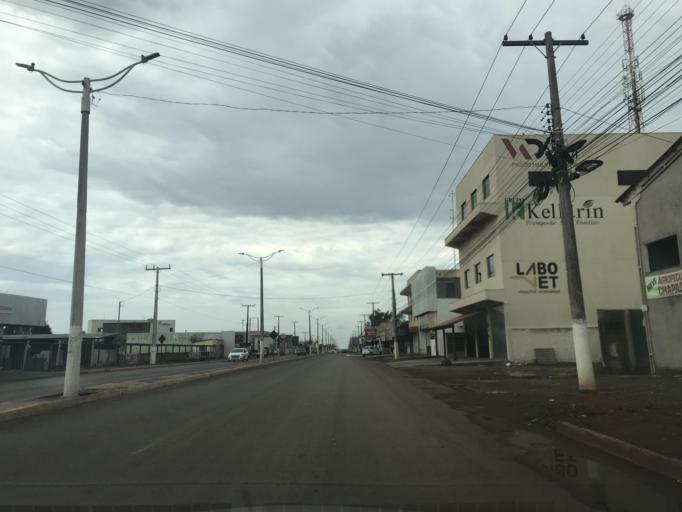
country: BR
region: Goias
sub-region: Luziania
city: Luziania
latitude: -16.2348
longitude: -47.9413
